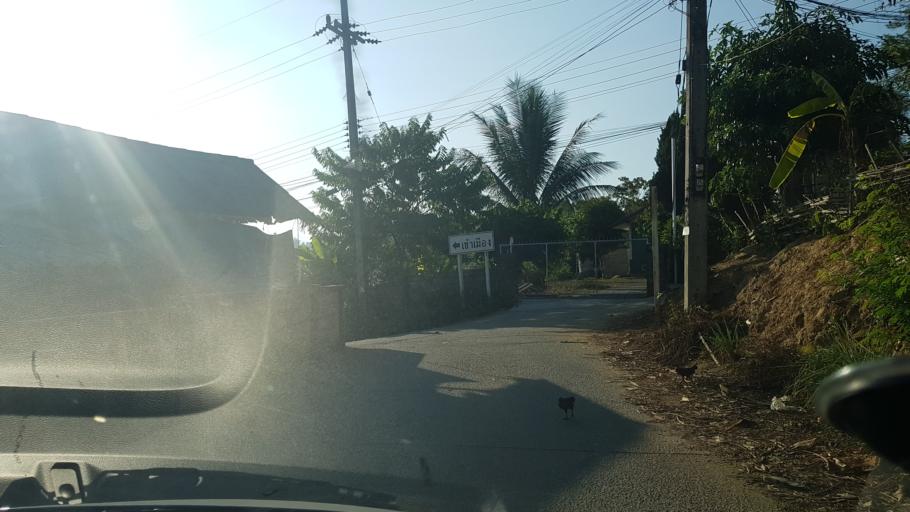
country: TH
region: Chiang Rai
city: Chiang Rai
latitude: 19.9452
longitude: 99.8053
